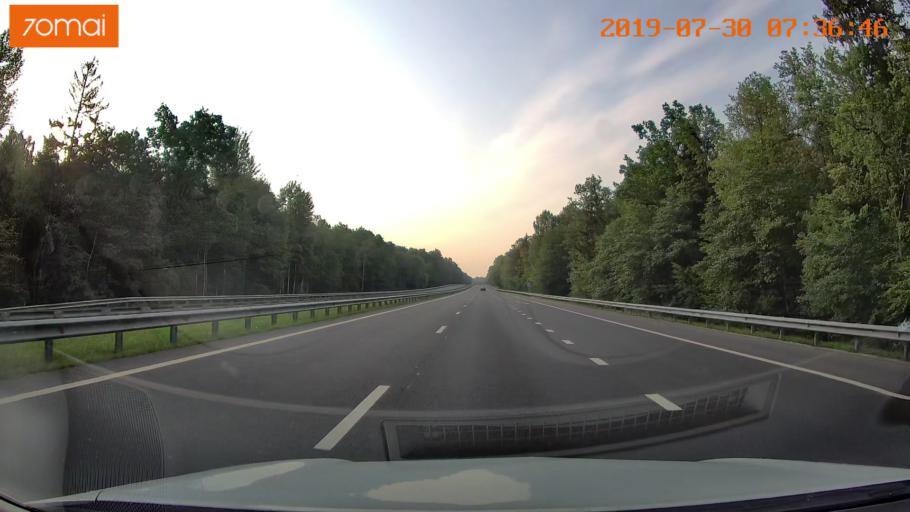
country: RU
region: Kaliningrad
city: Gvardeysk
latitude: 54.6616
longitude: 21.1318
